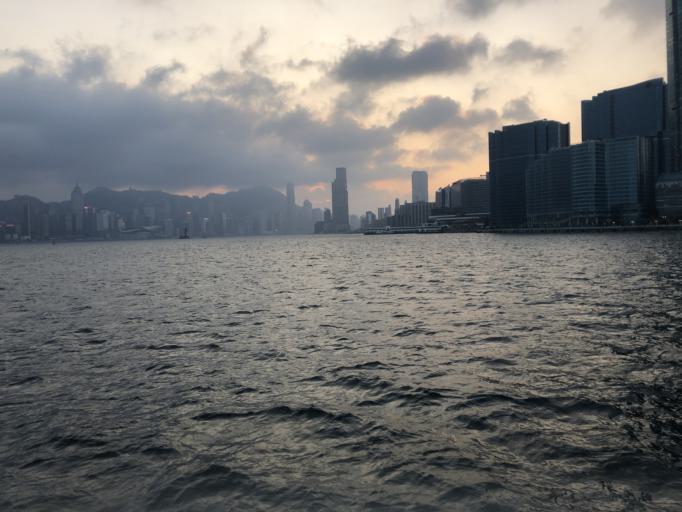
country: HK
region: Kowloon City
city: Kowloon
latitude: 22.3025
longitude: 114.1969
